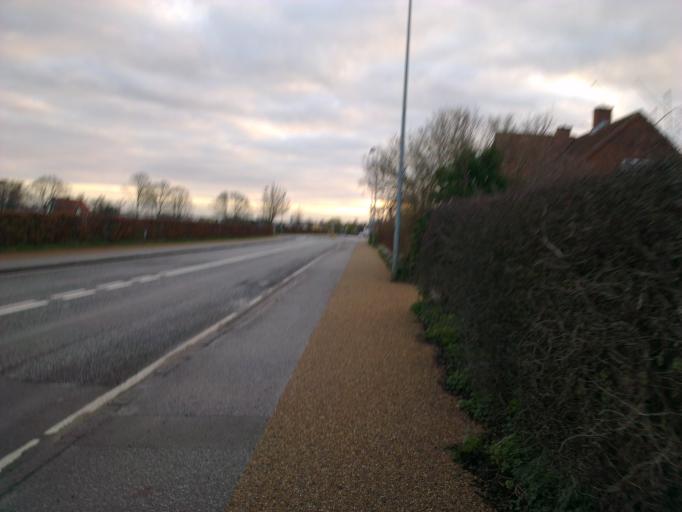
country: DK
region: Capital Region
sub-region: Frederikssund Kommune
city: Jaegerspris
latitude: 55.8551
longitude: 11.9934
